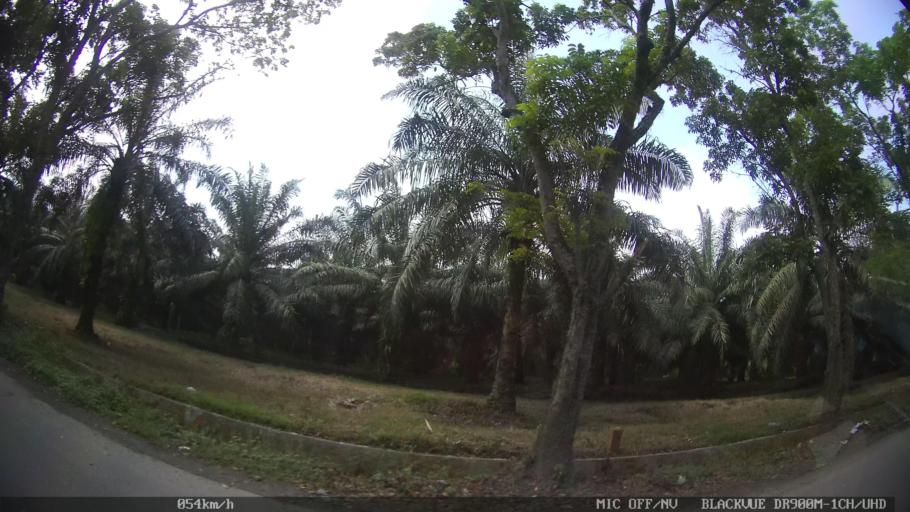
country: ID
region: North Sumatra
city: Binjai
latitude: 3.6513
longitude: 98.5311
